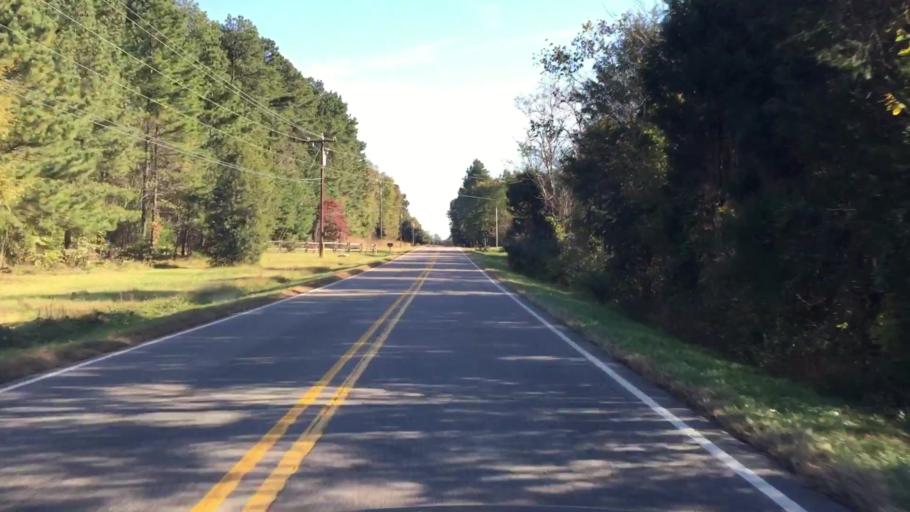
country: US
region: North Carolina
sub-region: Iredell County
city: Mooresville
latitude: 35.6142
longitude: -80.7520
